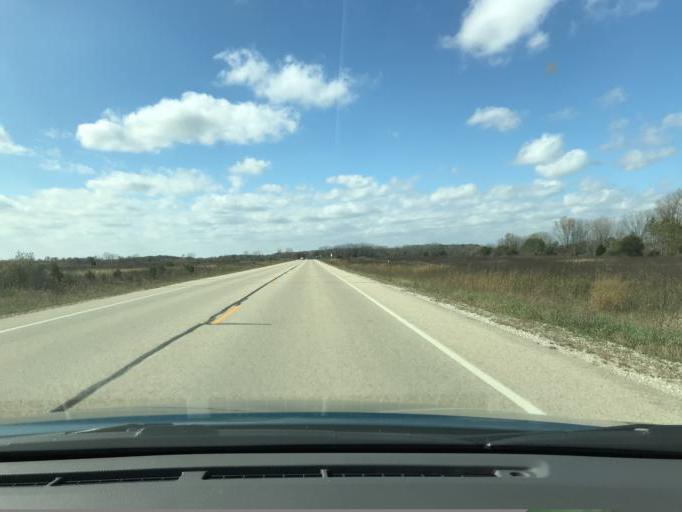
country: US
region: Wisconsin
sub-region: Kenosha County
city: Paddock Lake
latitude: 42.6359
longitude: -88.1406
